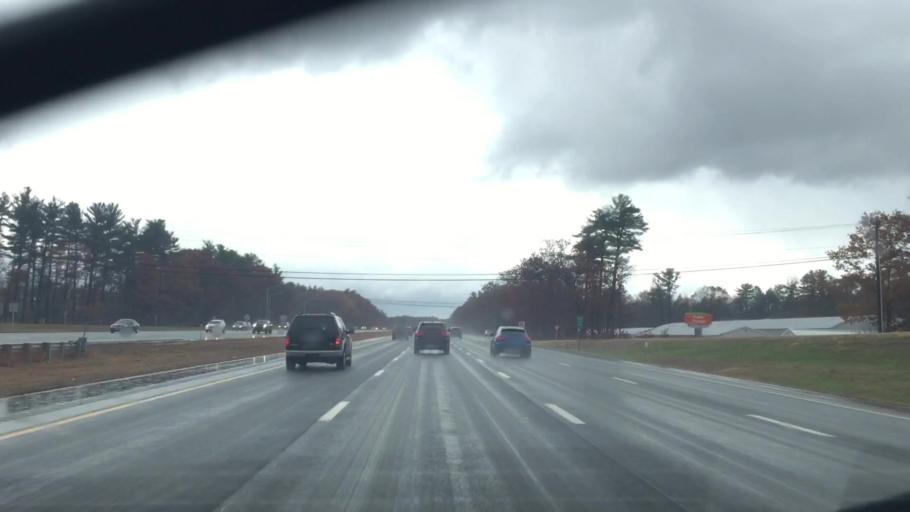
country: US
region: New Hampshire
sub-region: Rockingham County
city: Seabrook
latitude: 42.8948
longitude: -70.8797
